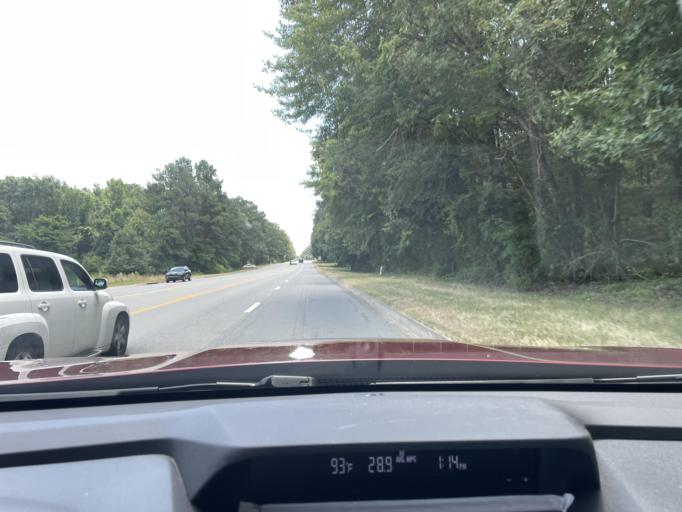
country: US
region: Arkansas
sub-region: Drew County
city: Monticello
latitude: 33.6576
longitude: -91.8030
